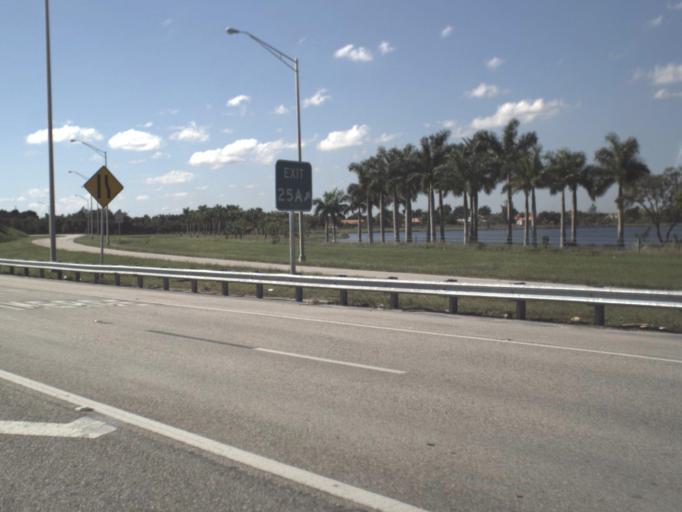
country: US
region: Florida
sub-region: Miami-Dade County
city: Sweetwater
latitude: 25.7777
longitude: -80.3861
